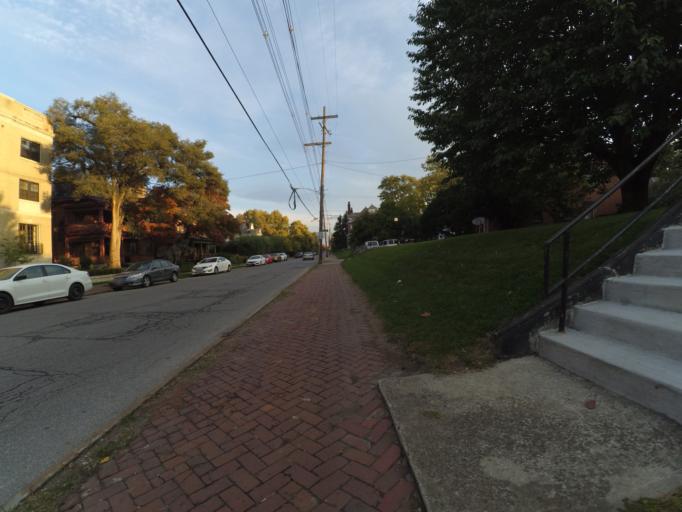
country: US
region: Ohio
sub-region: Franklin County
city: Columbus
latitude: 39.9776
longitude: -83.0089
